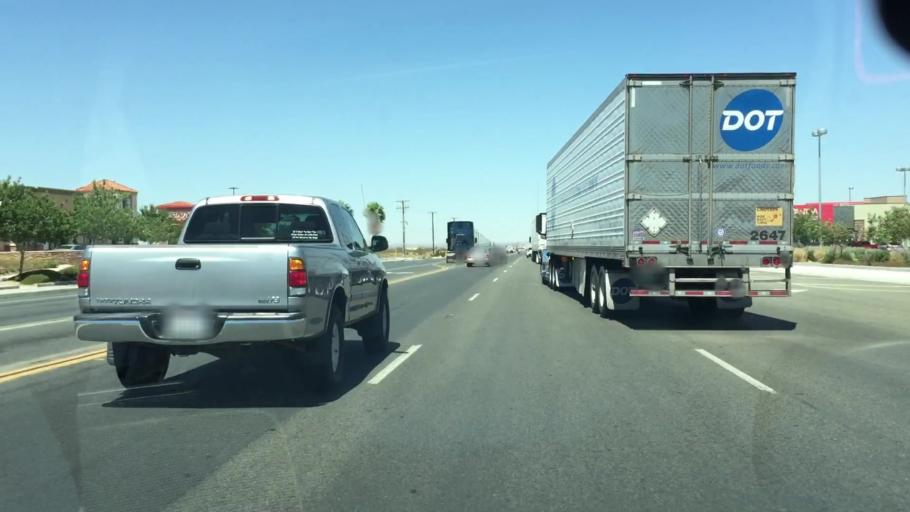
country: US
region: California
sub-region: San Bernardino County
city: Mountain View Acres
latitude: 34.5090
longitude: -117.3995
